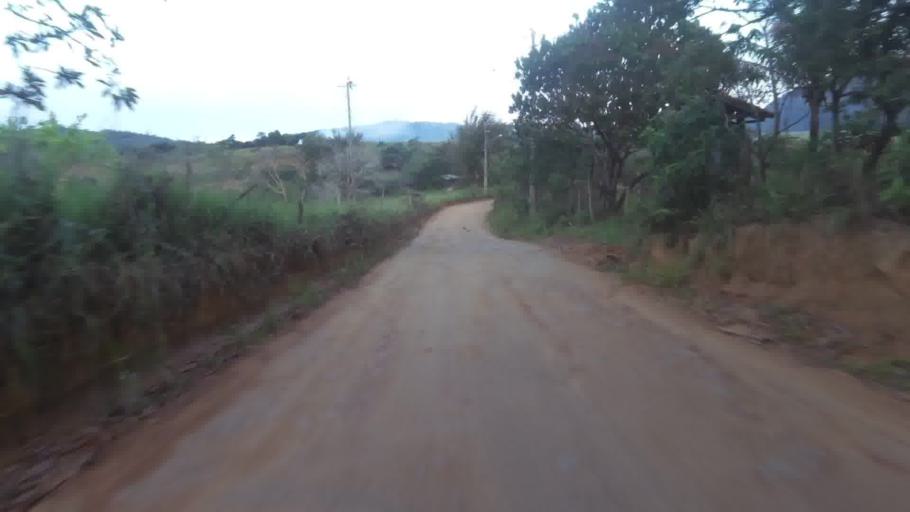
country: BR
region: Espirito Santo
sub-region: Guarapari
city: Guarapari
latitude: -20.7021
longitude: -40.5744
